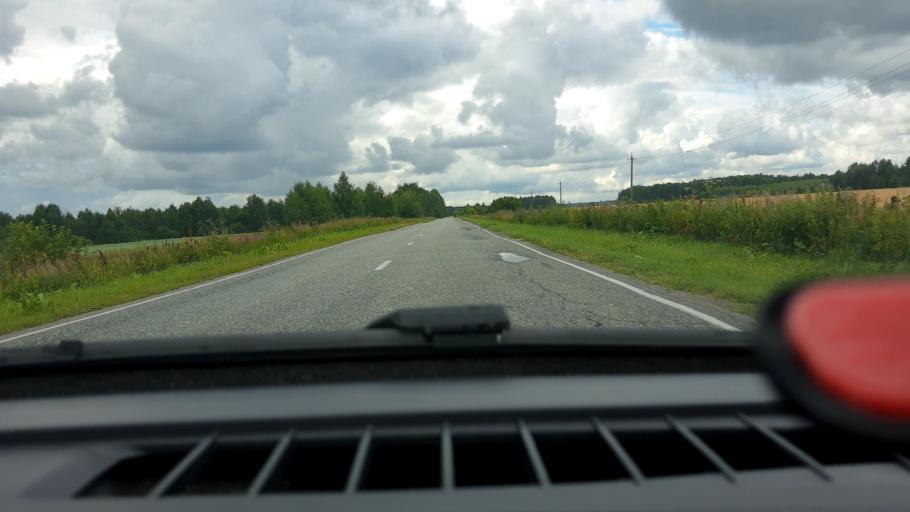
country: RU
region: Nizjnij Novgorod
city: Neklyudovo
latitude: 56.5193
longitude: 43.8989
